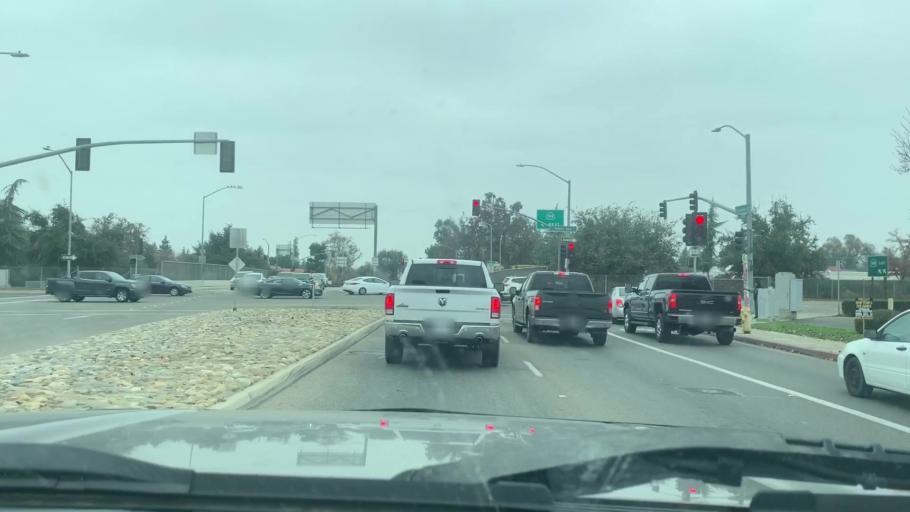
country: US
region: California
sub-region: Tulare County
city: Visalia
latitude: 36.3263
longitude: -119.3317
